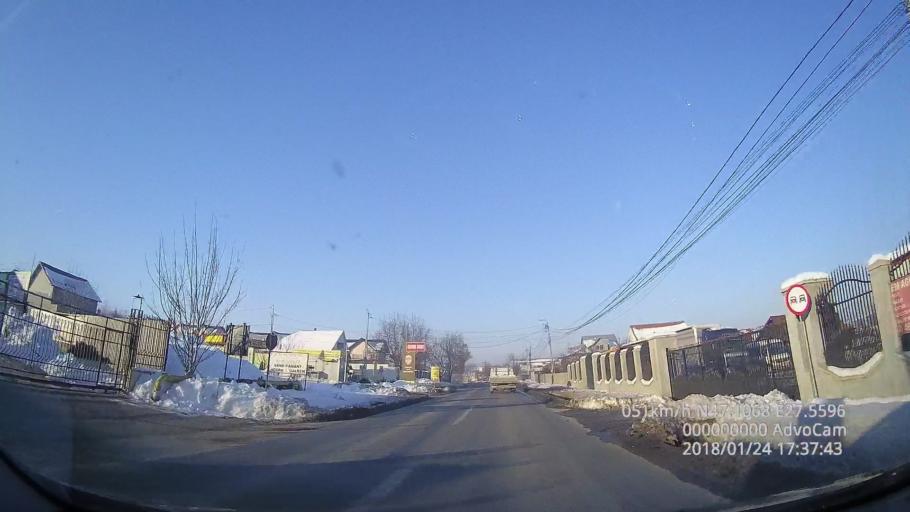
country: RO
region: Iasi
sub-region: Comuna Ciurea
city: Lunca Cetatuii
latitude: 47.1072
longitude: 27.5596
